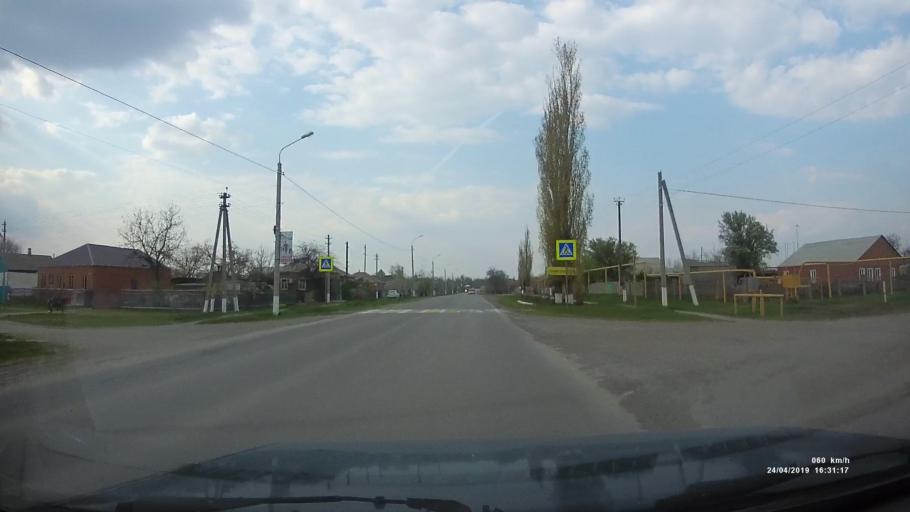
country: RU
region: Rostov
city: Orlovskiy
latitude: 46.8801
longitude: 42.0385
